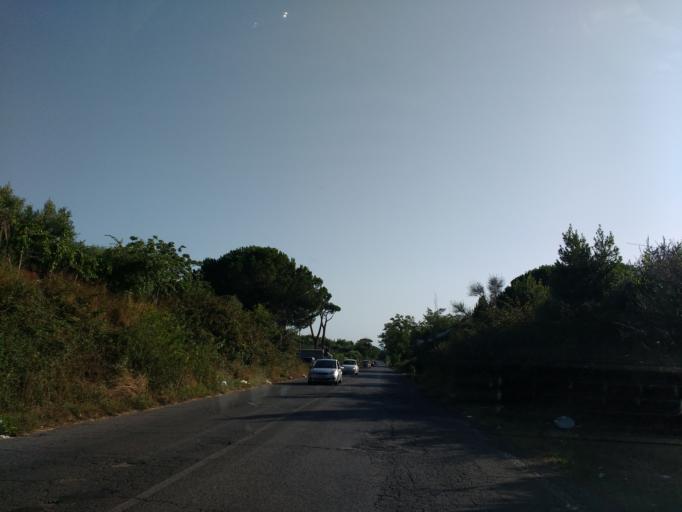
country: IT
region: Latium
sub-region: Citta metropolitana di Roma Capitale
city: Marino
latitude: 41.7578
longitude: 12.6411
